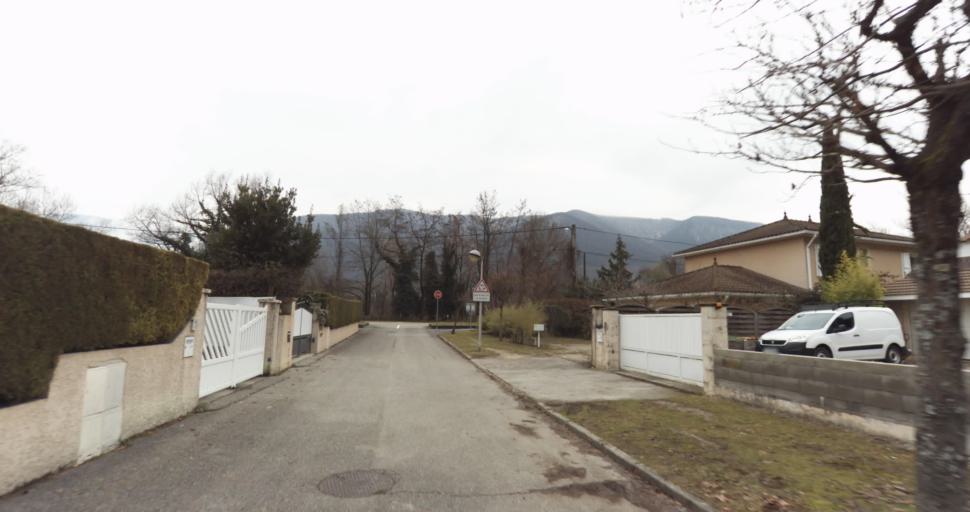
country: FR
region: Rhone-Alpes
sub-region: Departement de l'Isere
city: Vif
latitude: 45.0447
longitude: 5.6587
